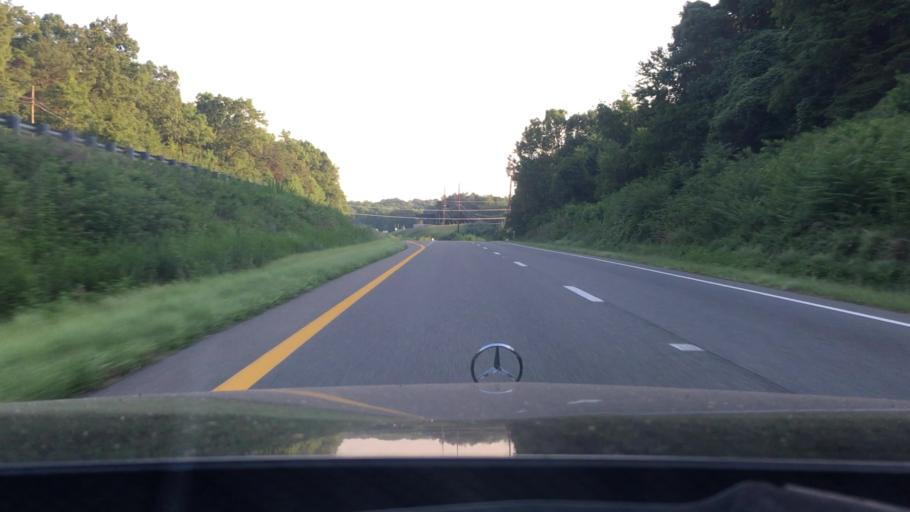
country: US
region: Virginia
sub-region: Pittsylvania County
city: Motley
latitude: 37.0511
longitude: -79.3556
